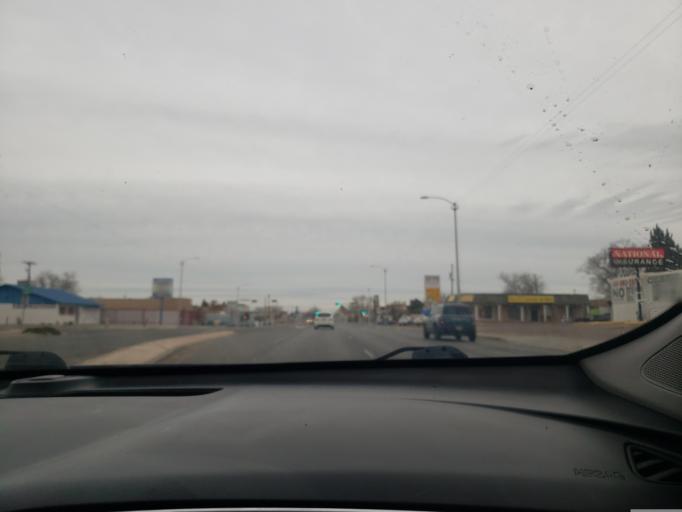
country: US
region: New Mexico
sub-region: Bernalillo County
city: North Valley
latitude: 35.1220
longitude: -106.5864
